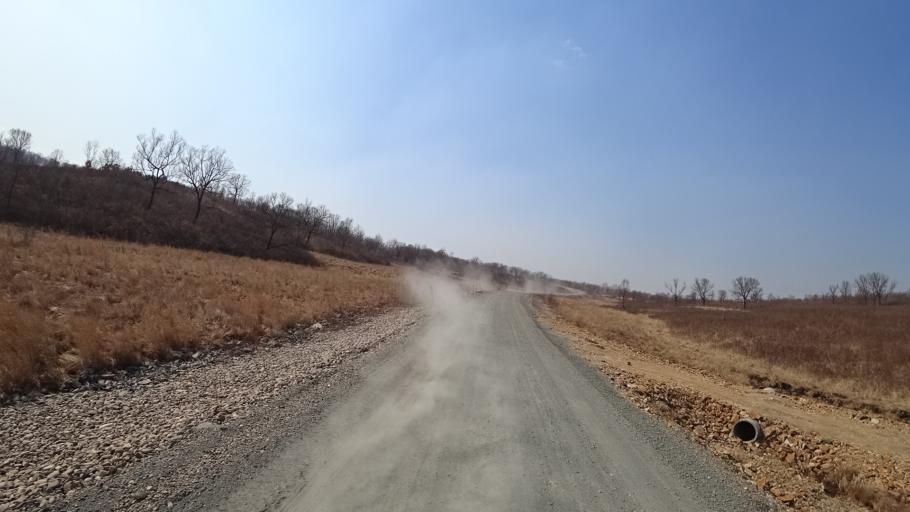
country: RU
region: Amur
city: Novobureyskiy
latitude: 49.8225
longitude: 129.9984
